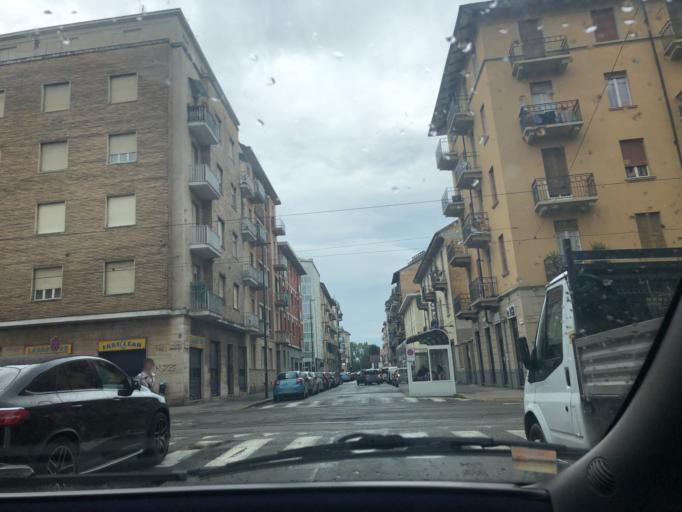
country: IT
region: Piedmont
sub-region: Provincia di Torino
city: Lesna
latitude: 45.0810
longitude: 7.6412
